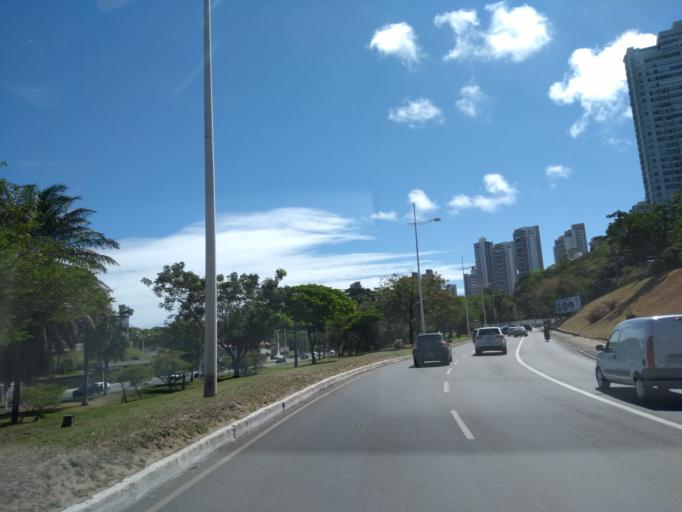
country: BR
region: Bahia
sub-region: Salvador
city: Salvador
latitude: -12.9995
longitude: -38.4804
